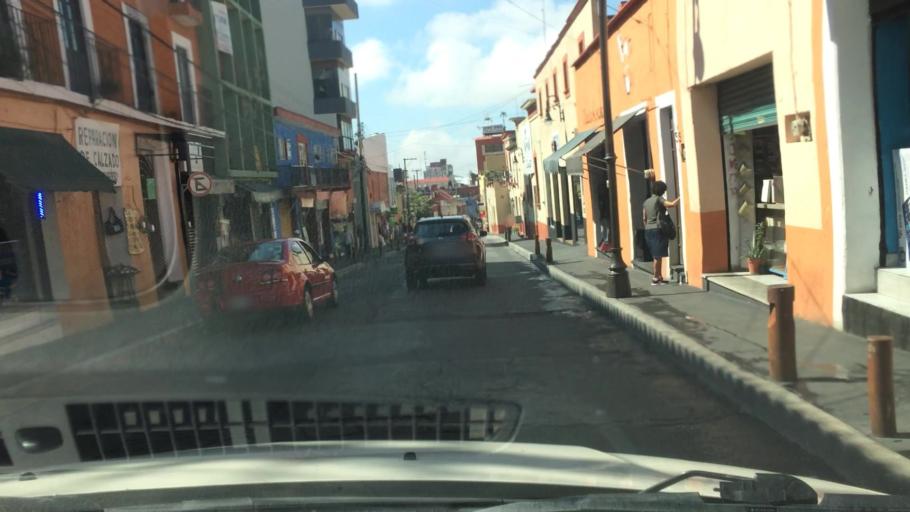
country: MX
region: Morelos
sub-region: Cuernavaca
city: Cuernavaca
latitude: 18.9269
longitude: -99.2375
